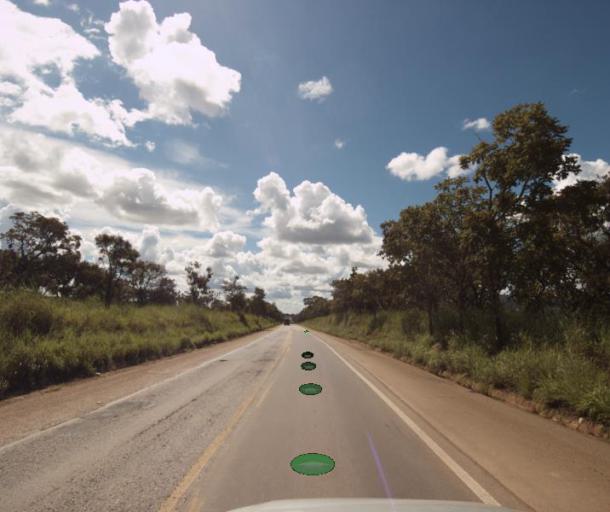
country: BR
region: Goias
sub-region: Porangatu
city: Porangatu
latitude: -13.6791
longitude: -49.0241
